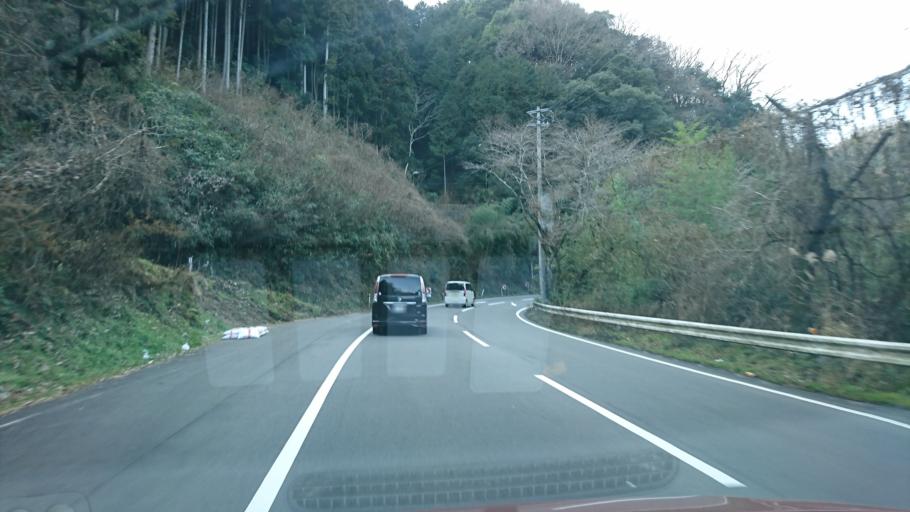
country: JP
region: Ehime
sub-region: Shikoku-chuo Shi
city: Matsuyama
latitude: 33.8969
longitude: 132.8575
